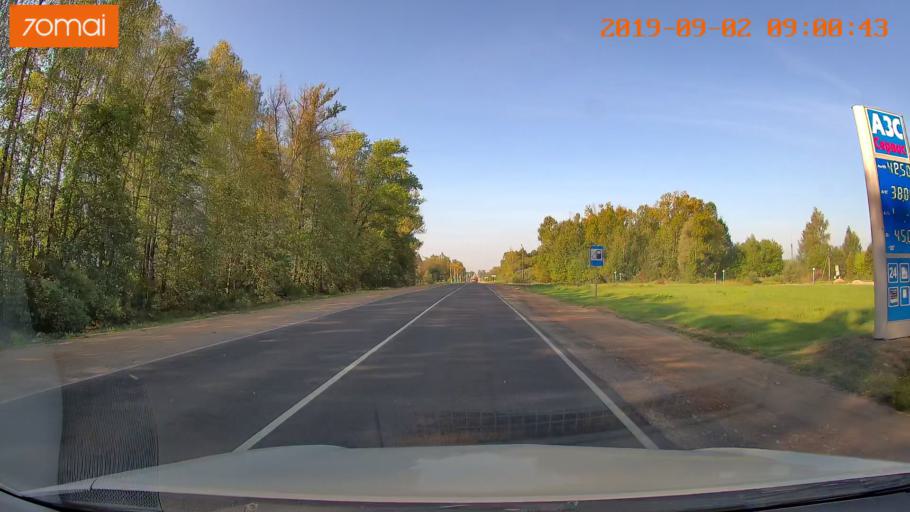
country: RU
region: Kaluga
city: Myatlevo
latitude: 54.9104
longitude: 35.7001
